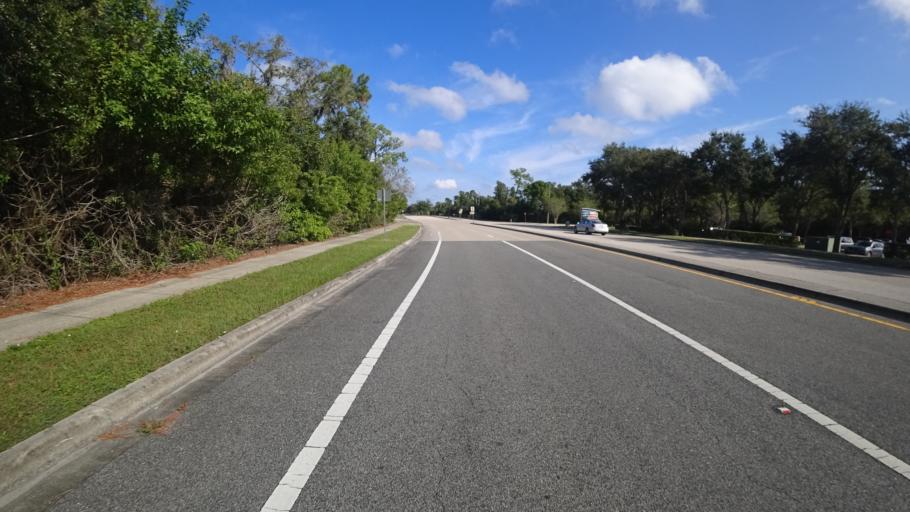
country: US
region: Florida
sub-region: Sarasota County
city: The Meadows
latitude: 27.3913
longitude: -82.4632
